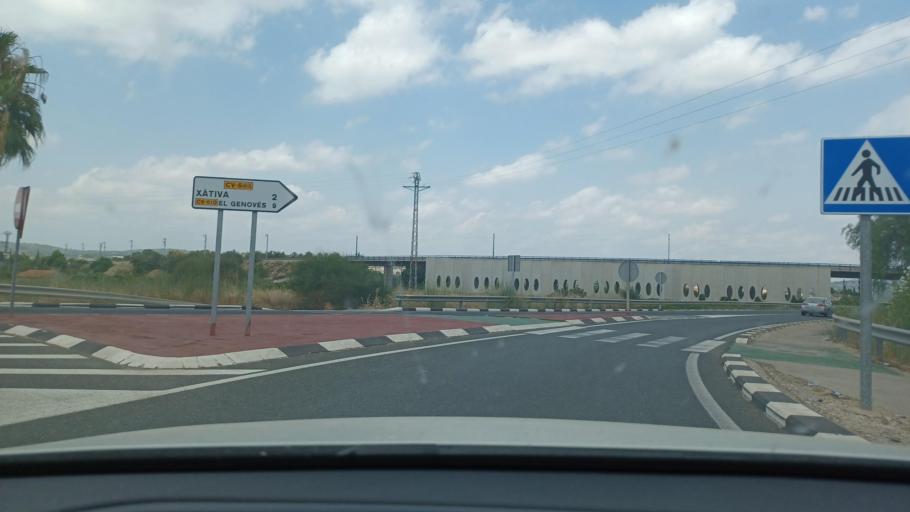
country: ES
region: Valencia
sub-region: Provincia de Valencia
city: Valles
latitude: 38.9782
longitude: -0.5531
